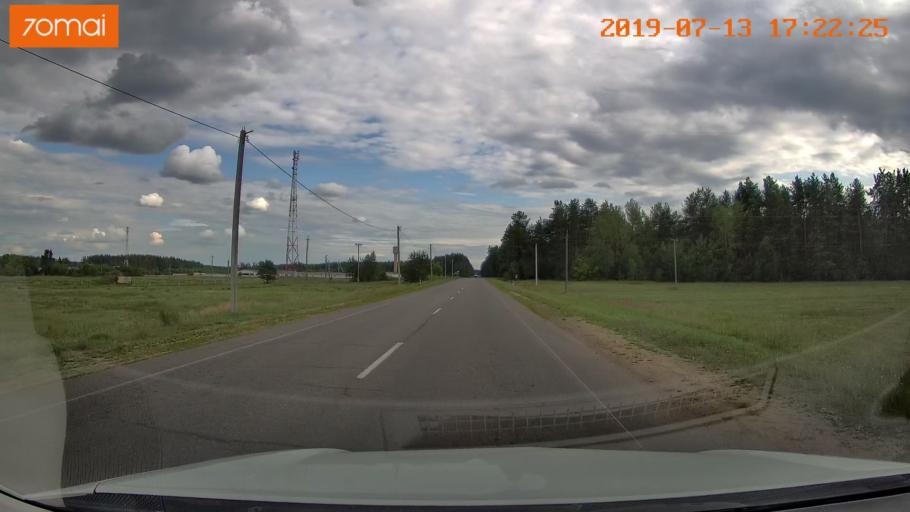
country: BY
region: Mogilev
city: Babruysk
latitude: 53.2713
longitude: 29.2343
